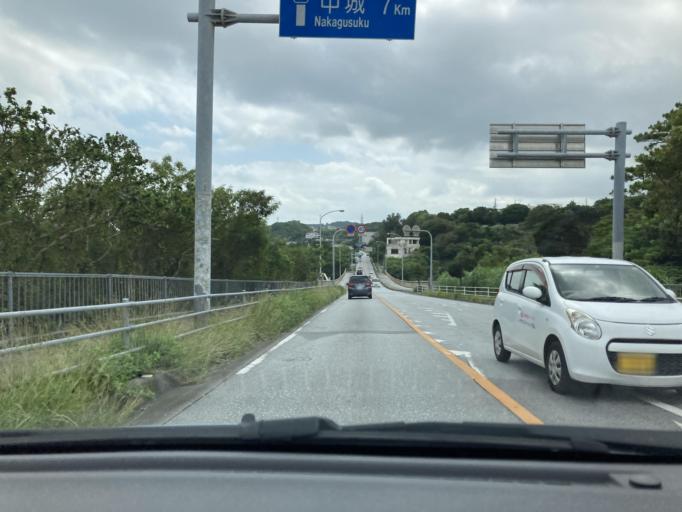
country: JP
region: Okinawa
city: Chatan
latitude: 26.2955
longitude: 127.7845
